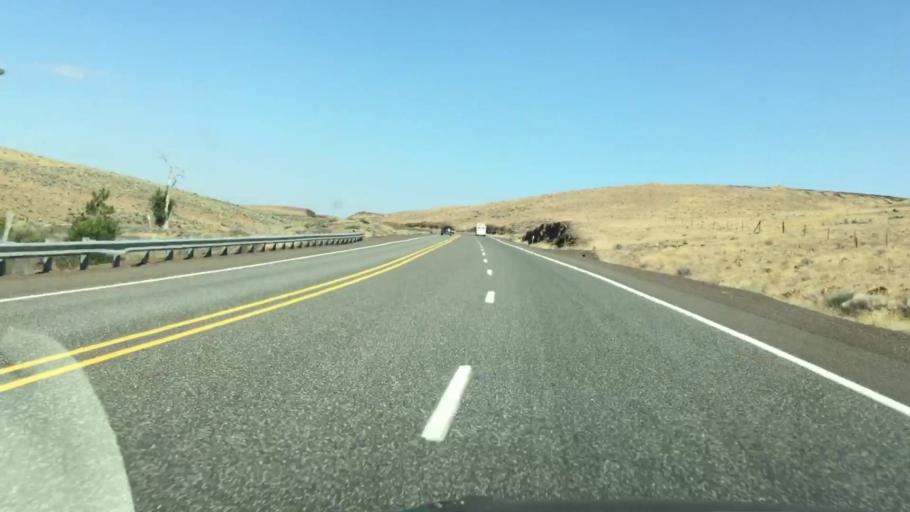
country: US
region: Oregon
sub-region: Wasco County
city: The Dalles
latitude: 45.3141
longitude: -121.1468
